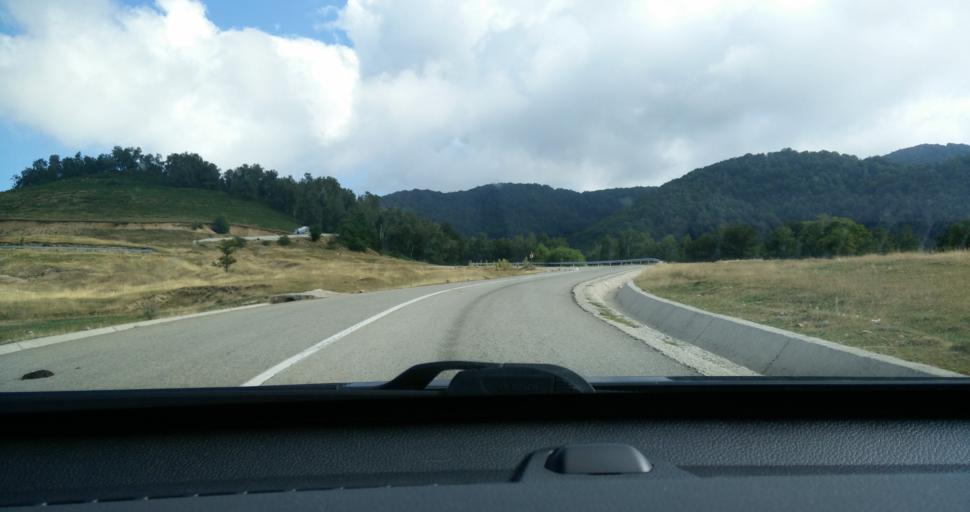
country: RO
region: Gorj
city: Novaci-Straini
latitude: 45.2173
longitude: 23.6984
